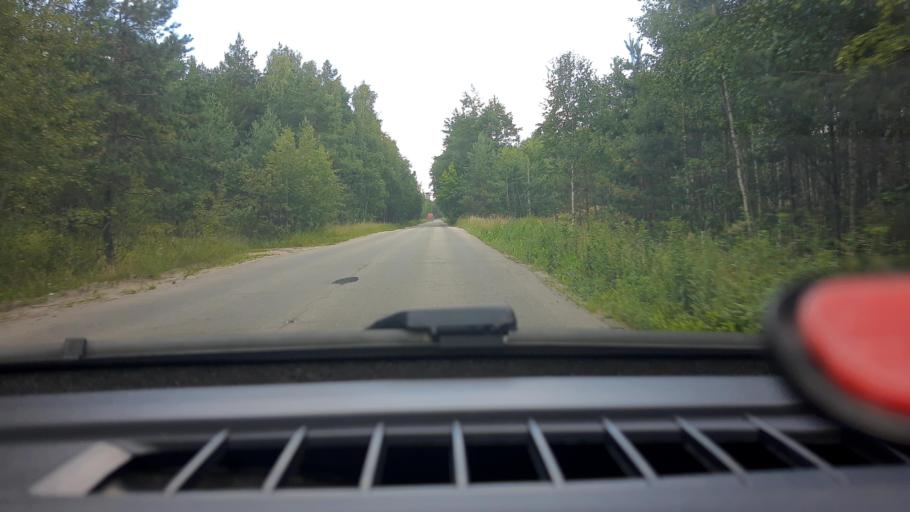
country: RU
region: Nizjnij Novgorod
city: Babino
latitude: 56.3183
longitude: 43.6262
